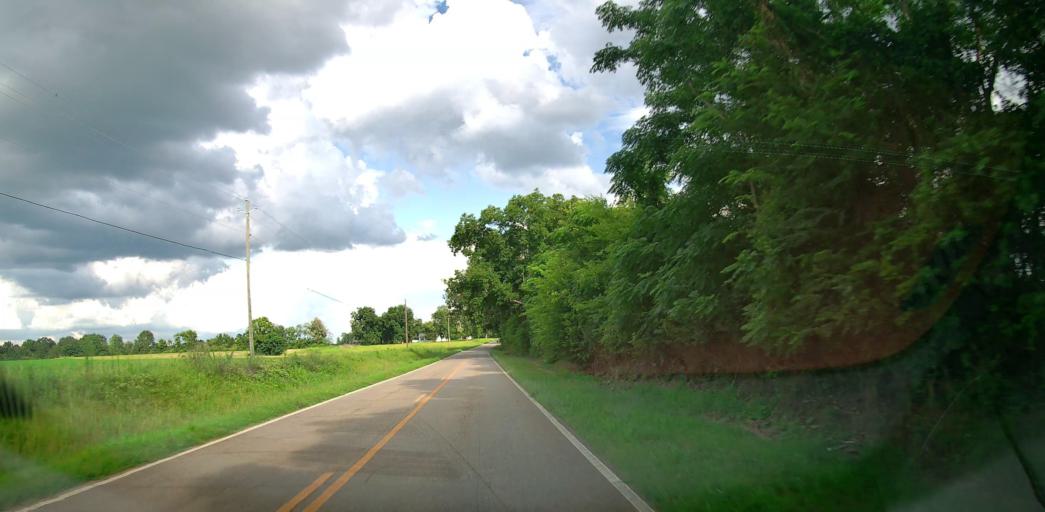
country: US
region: Georgia
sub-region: Bleckley County
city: Cochran
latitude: 32.4068
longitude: -83.3834
